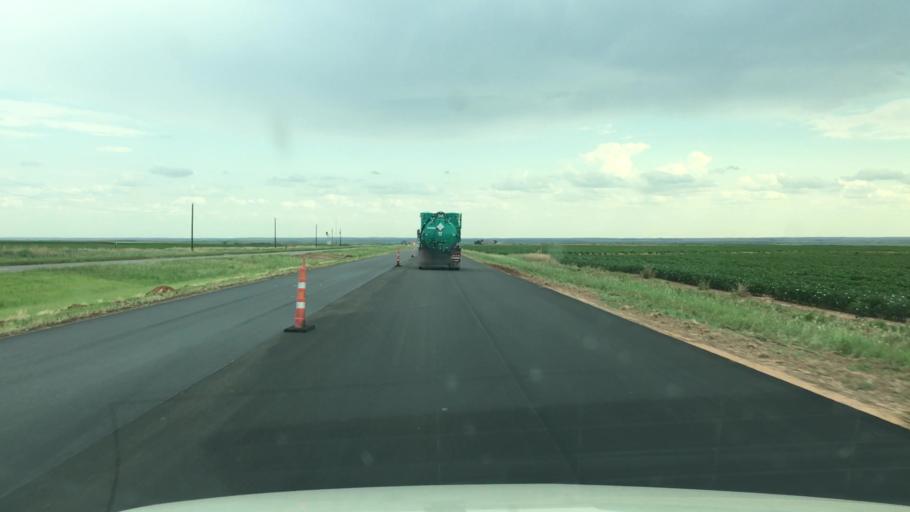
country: US
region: Texas
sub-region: Hall County
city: Memphis
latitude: 34.6294
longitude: -100.4756
